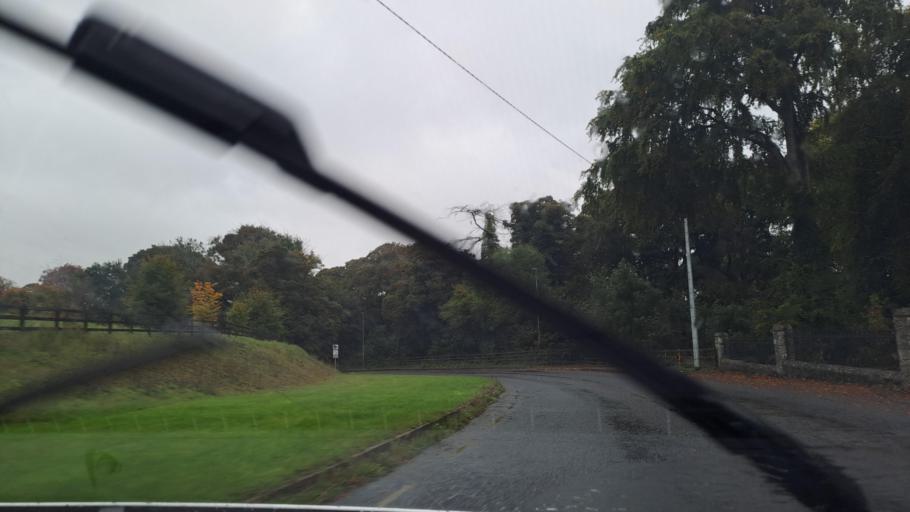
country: IE
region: Ulster
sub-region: County Monaghan
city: Carrickmacross
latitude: 53.9684
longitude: -6.7001
